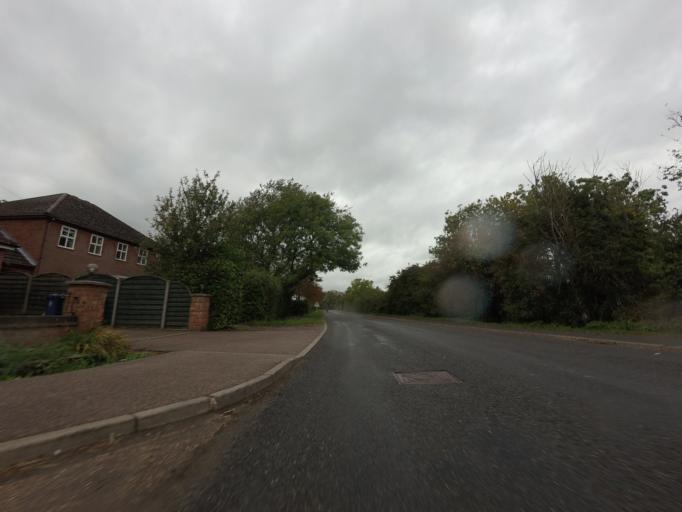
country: GB
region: England
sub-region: Cambridgeshire
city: Comberton
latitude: 52.1593
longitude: 0.0013
